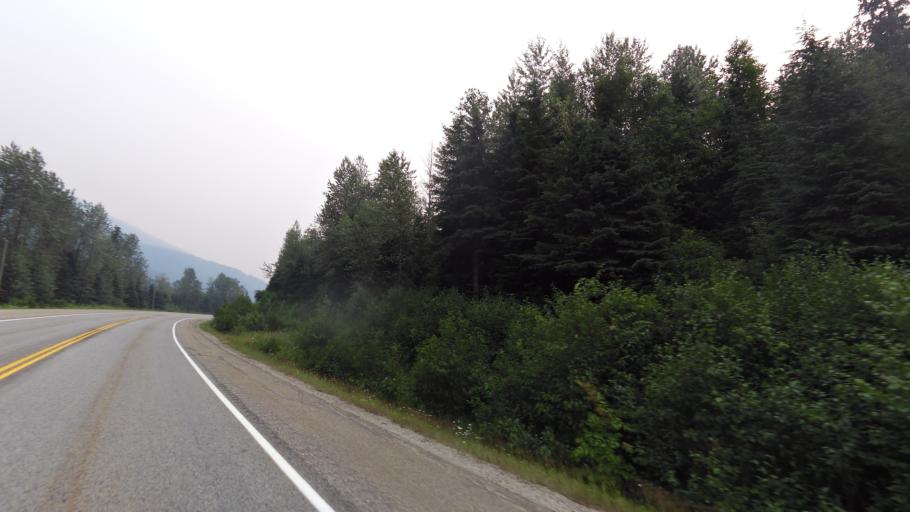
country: CA
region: Alberta
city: Jasper Park Lodge
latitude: 52.3306
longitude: -119.1774
